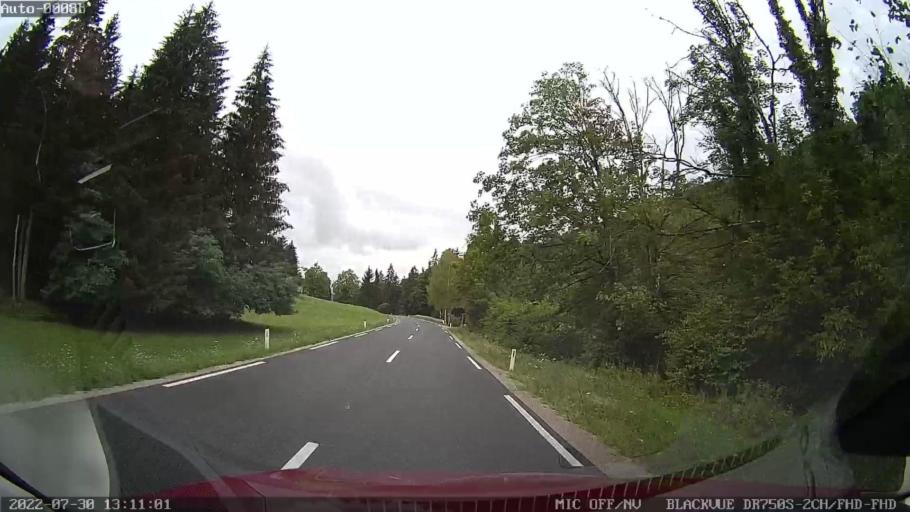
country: SI
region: Dolenjske Toplice
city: Dolenjske Toplice
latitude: 45.6998
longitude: 15.0824
